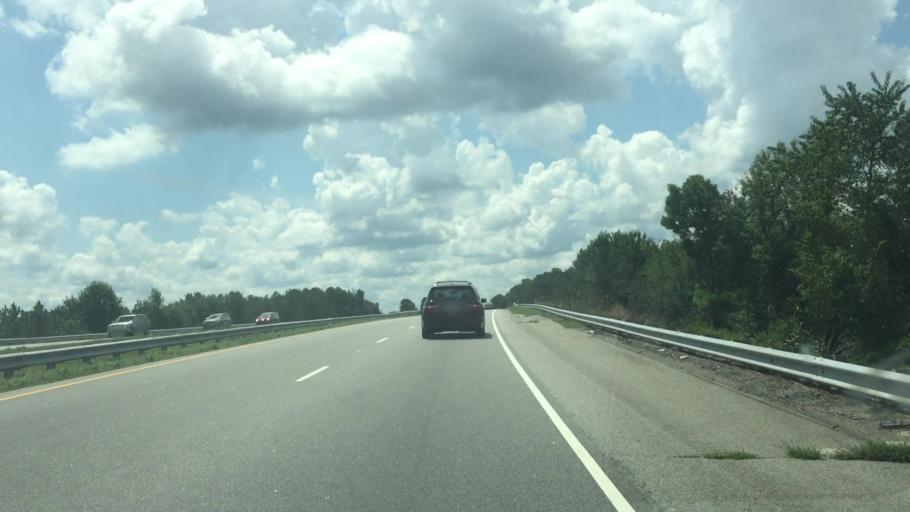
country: US
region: North Carolina
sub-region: Scotland County
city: Laurel Hill
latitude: 34.8342
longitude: -79.5957
